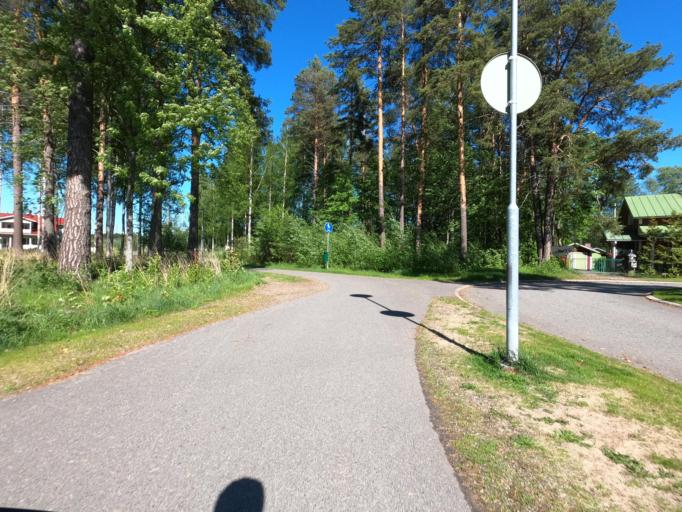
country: FI
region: North Karelia
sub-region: Joensuu
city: Joensuu
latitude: 62.5757
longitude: 29.7721
